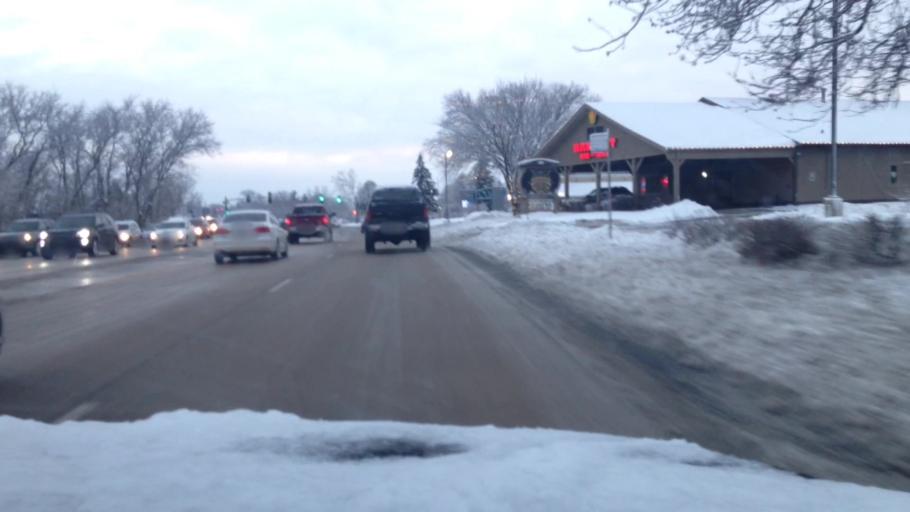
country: US
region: Illinois
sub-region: Kane County
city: South Elgin
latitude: 42.0203
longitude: -88.3134
